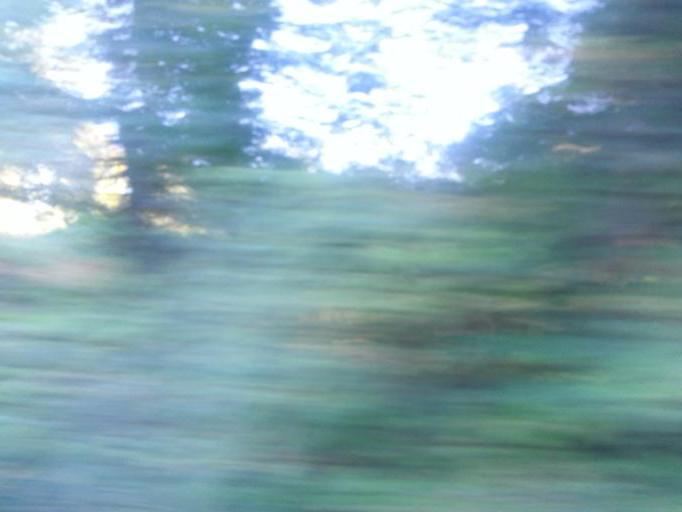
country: US
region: Tennessee
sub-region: Knox County
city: Knoxville
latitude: 35.9016
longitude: -83.8401
